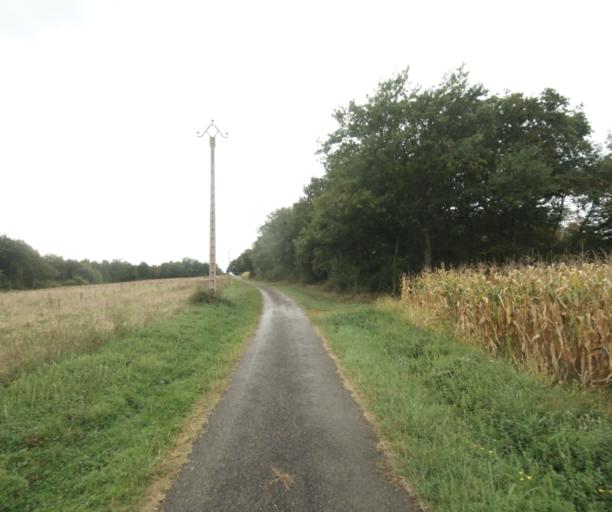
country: FR
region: Midi-Pyrenees
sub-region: Departement du Gers
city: Cazaubon
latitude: 43.8965
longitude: -0.1183
